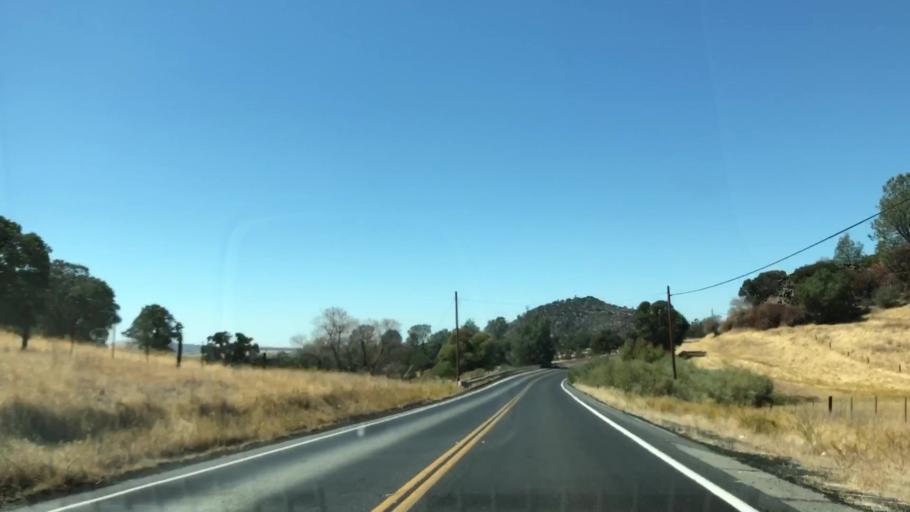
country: US
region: California
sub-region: Tuolumne County
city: Jamestown
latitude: 37.8870
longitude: -120.5088
